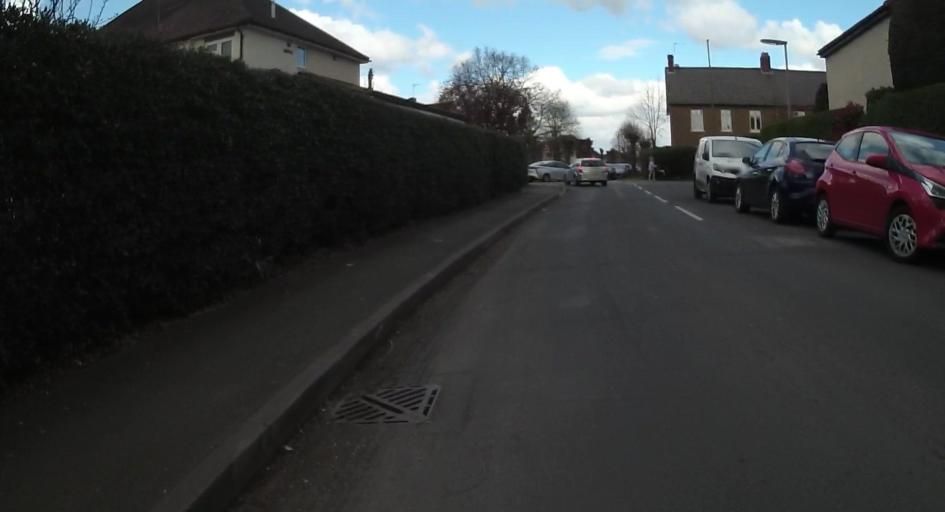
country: GB
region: England
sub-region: Surrey
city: Addlestone
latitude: 51.3687
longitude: -0.4997
